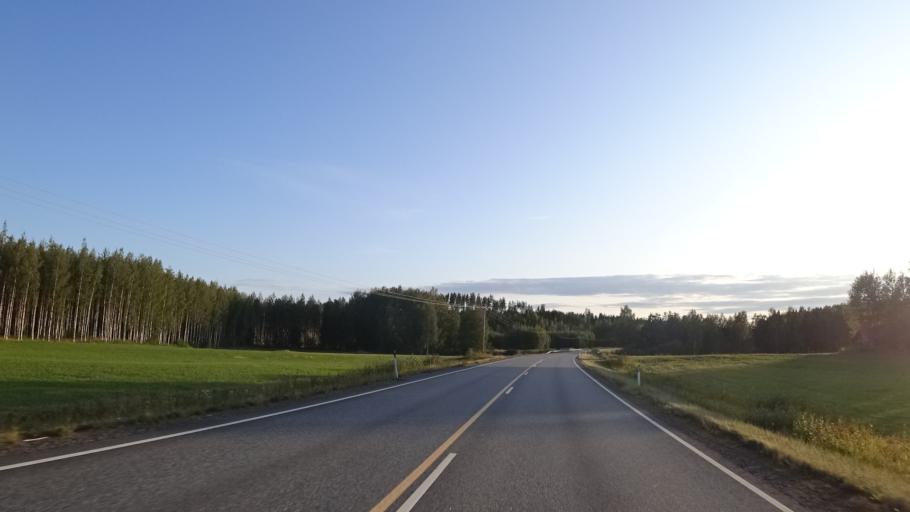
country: FI
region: South Karelia
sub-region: Lappeenranta
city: Ylaemaa
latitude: 60.7925
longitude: 28.0263
